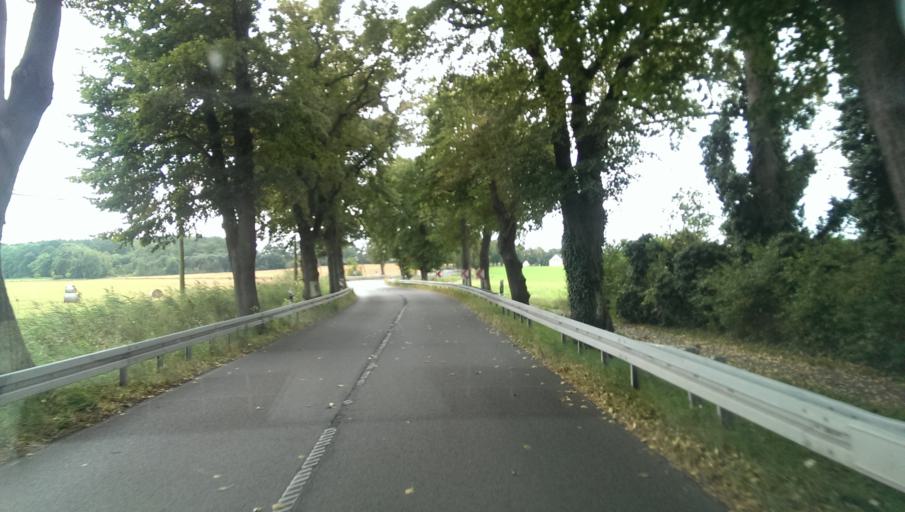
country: DE
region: Brandenburg
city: Trebbin
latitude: 52.2061
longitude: 13.2104
